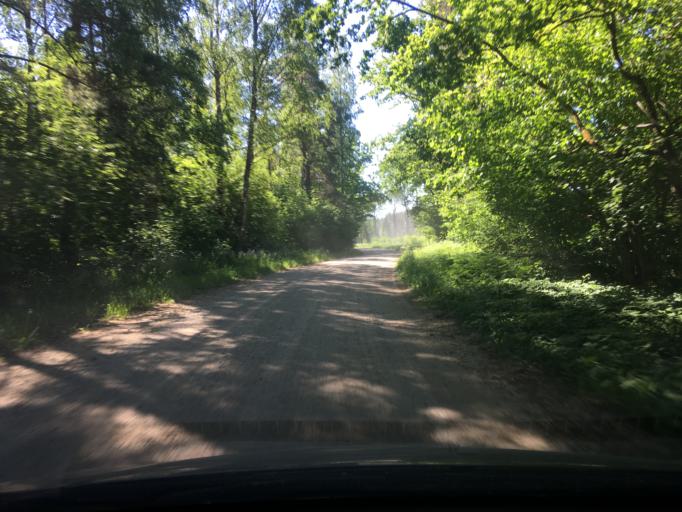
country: EE
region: Laeaene
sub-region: Lihula vald
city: Lihula
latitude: 58.6430
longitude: 23.7877
